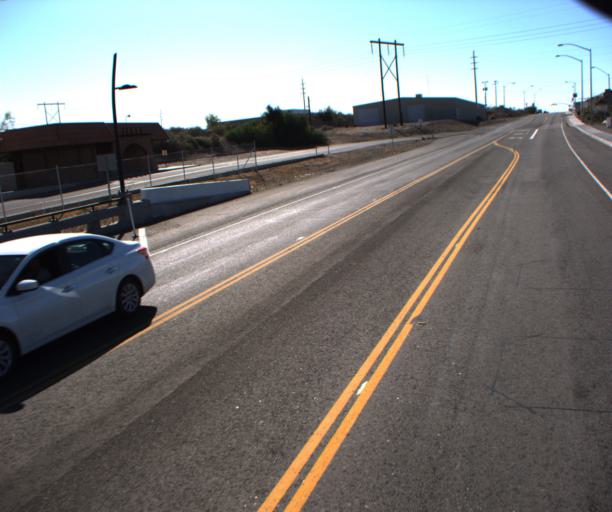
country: US
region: Arizona
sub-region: La Paz County
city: Parker
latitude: 34.1586
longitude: -114.2977
